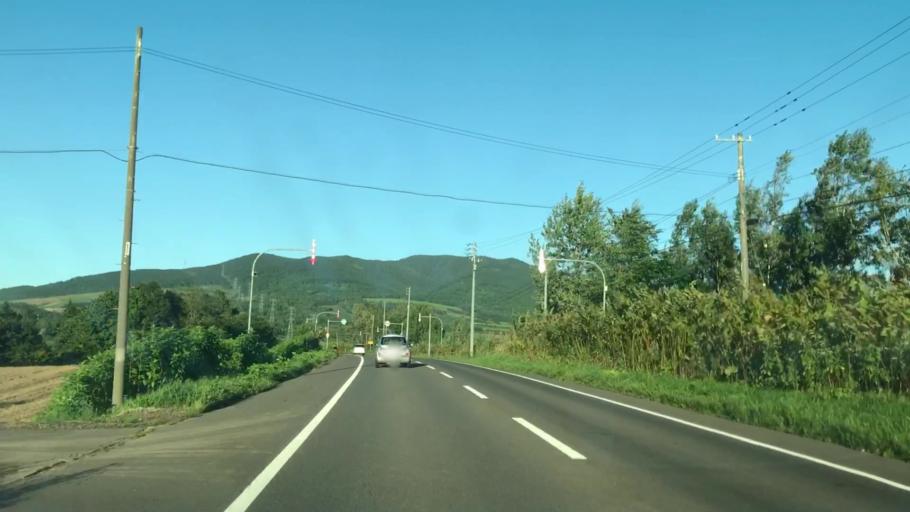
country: JP
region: Hokkaido
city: Niseko Town
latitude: 42.7039
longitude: 140.8545
